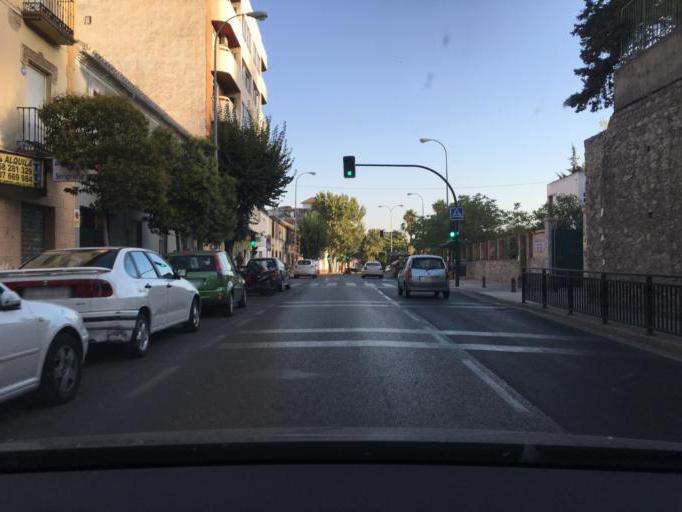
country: ES
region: Andalusia
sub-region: Provincia de Granada
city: Granada
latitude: 37.1886
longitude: -3.6003
